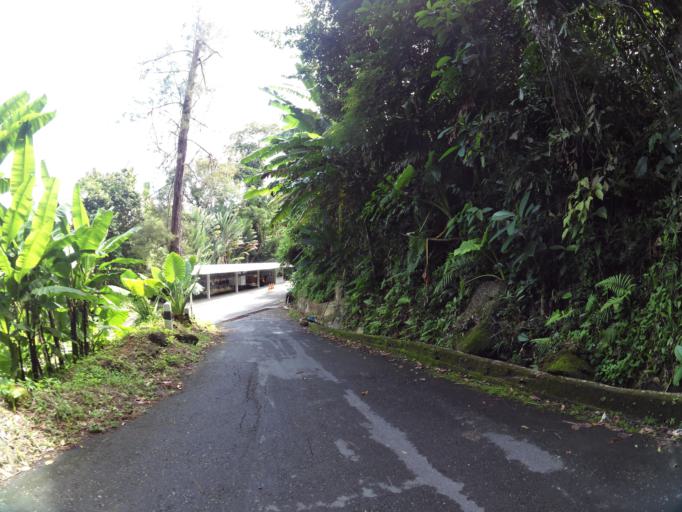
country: TH
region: Phuket
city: Patong
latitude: 7.8862
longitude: 98.2826
